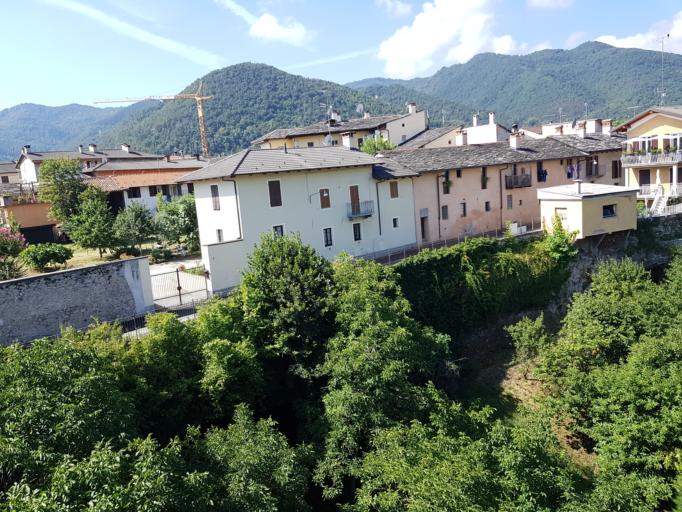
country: IT
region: Piedmont
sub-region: Provincia di Cuneo
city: Dronero
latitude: 44.4645
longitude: 7.3663
